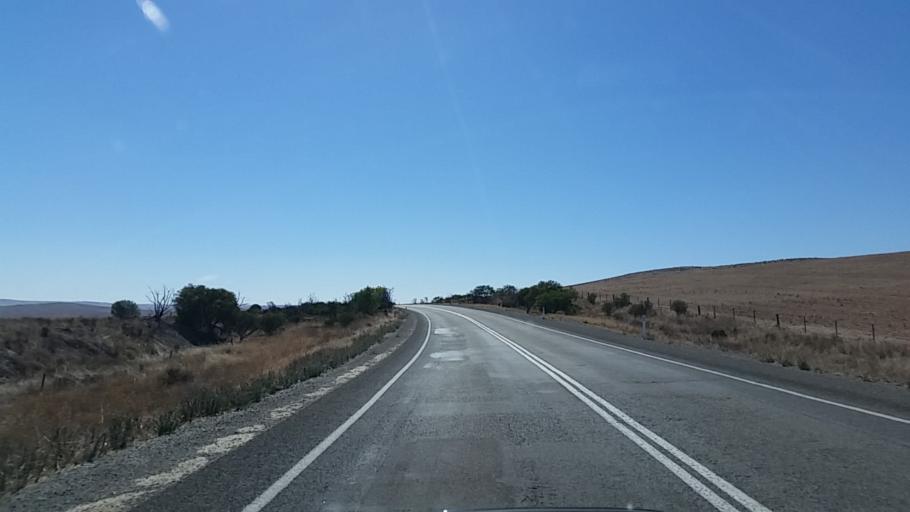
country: AU
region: South Australia
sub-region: Northern Areas
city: Jamestown
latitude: -33.3285
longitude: 138.8887
